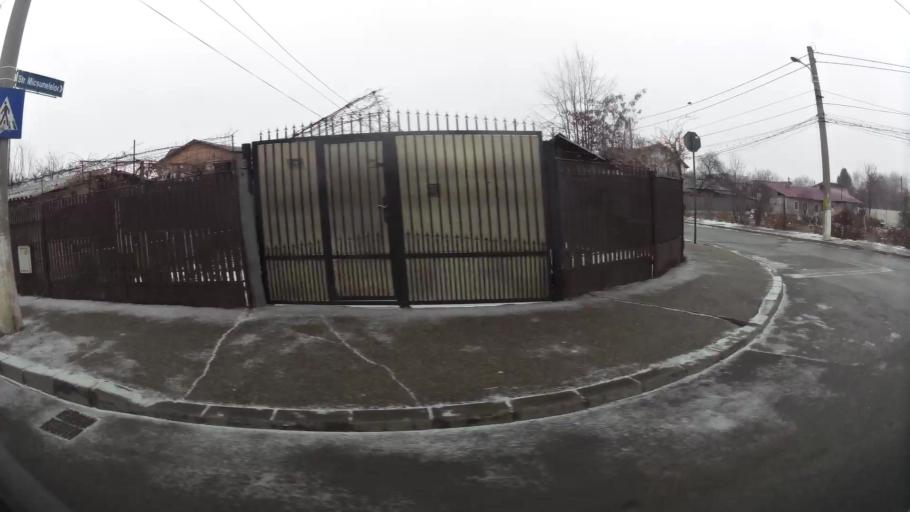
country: RO
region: Prahova
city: Ploiesti
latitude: 44.9536
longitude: 26.0433
